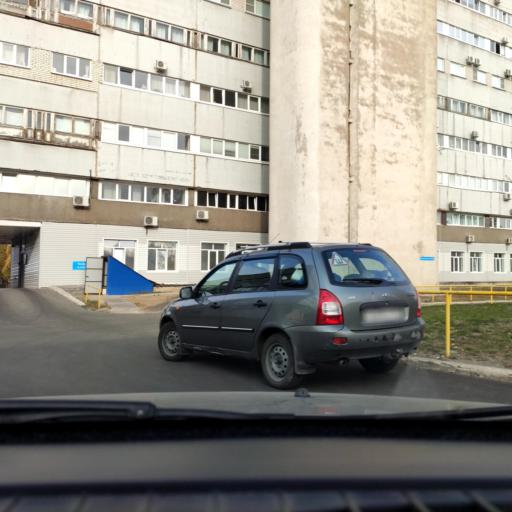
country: RU
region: Samara
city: Tol'yatti
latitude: 53.5221
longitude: 49.3255
